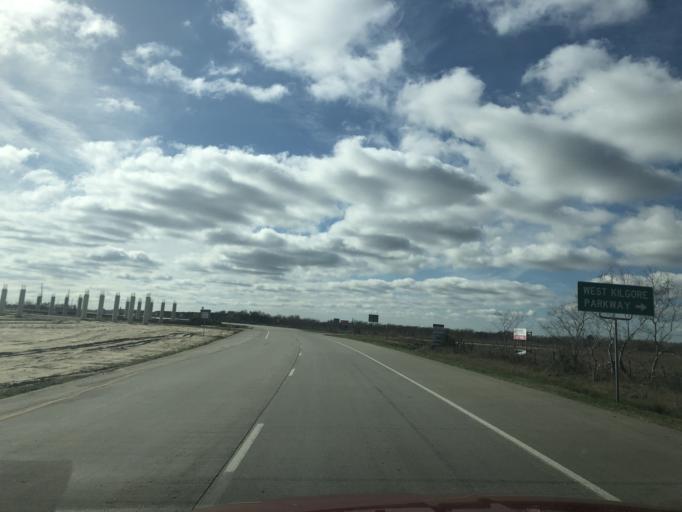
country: US
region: Texas
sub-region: Chambers County
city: Mont Belvieu
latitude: 29.8046
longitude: -94.8678
